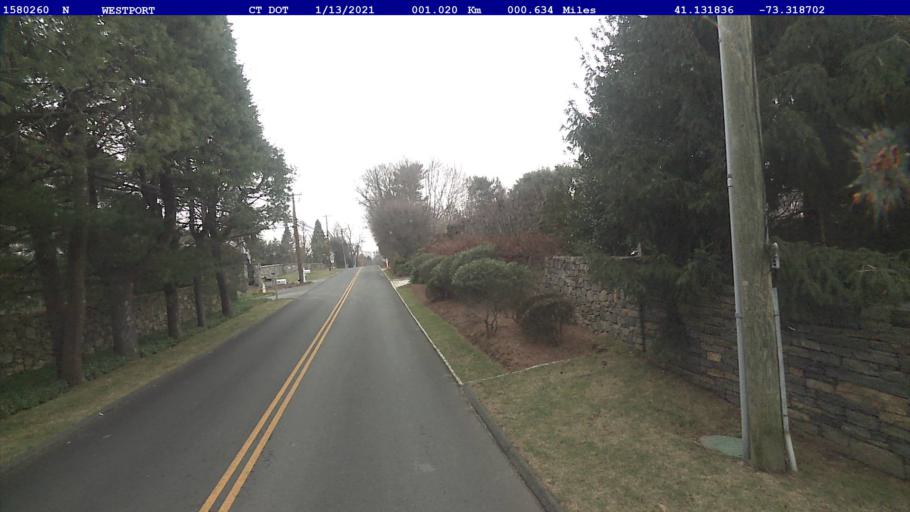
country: US
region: Connecticut
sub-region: Fairfield County
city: Southport
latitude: 41.1318
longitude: -73.3187
